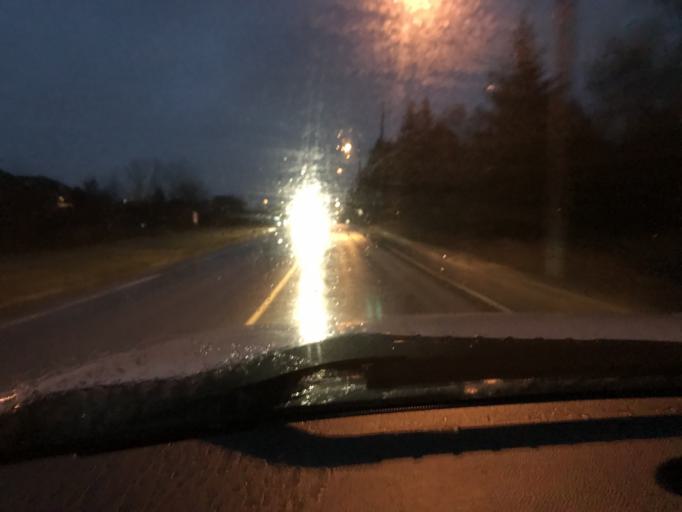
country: CA
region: Ontario
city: Waterloo
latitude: 43.4905
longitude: -80.5801
